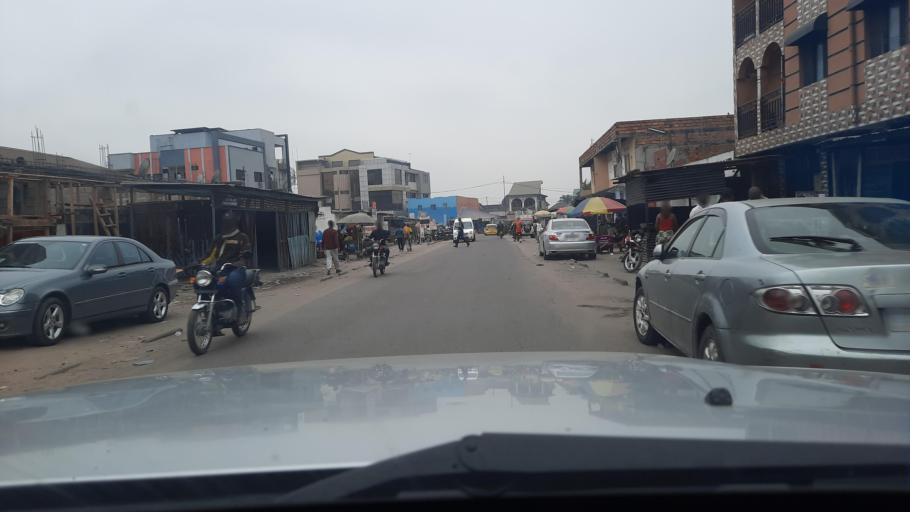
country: CD
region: Kinshasa
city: Kinshasa
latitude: -4.3362
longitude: 15.3181
